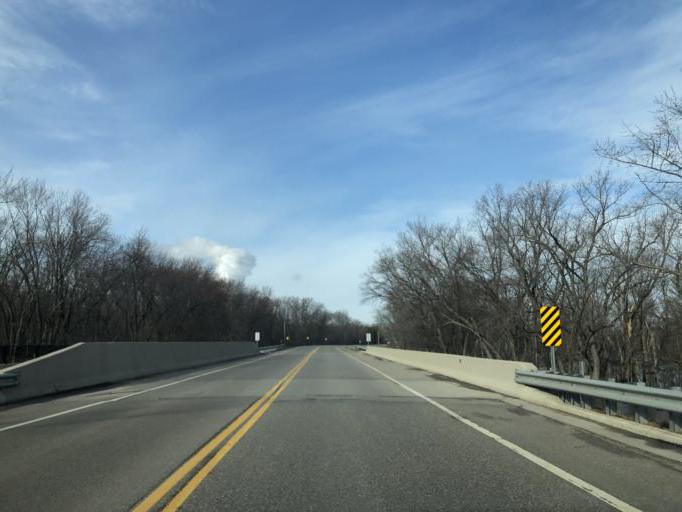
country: US
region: Minnesota
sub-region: Sherburne County
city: Becker
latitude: 45.3942
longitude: -93.8523
